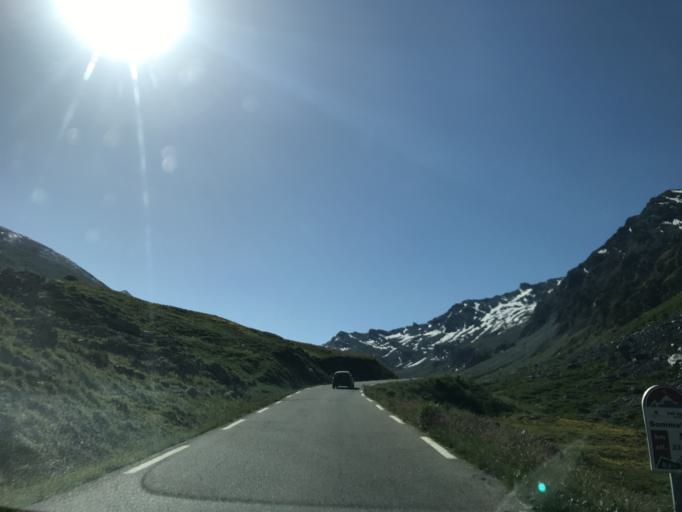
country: IT
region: Piedmont
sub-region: Provincia di Cuneo
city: Pontechianale
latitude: 44.6967
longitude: 6.9482
